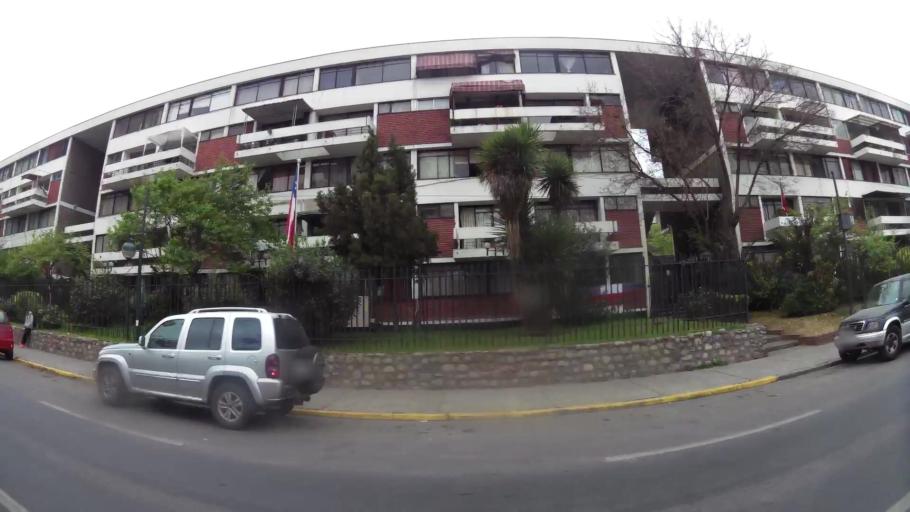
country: CL
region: Santiago Metropolitan
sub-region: Provincia de Santiago
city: Villa Presidente Frei, Nunoa, Santiago, Chile
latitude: -33.4563
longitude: -70.5836
